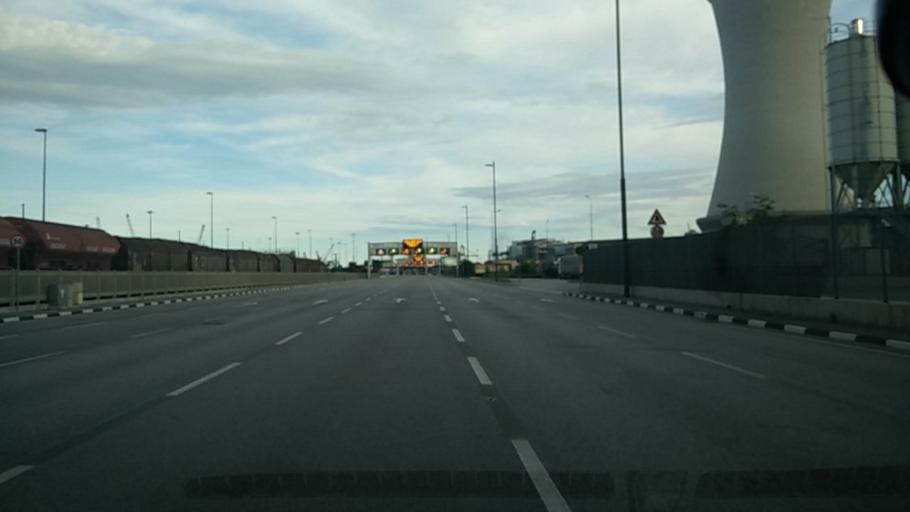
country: IT
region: Veneto
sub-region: Provincia di Venezia
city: Mestre
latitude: 45.4667
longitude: 12.2392
